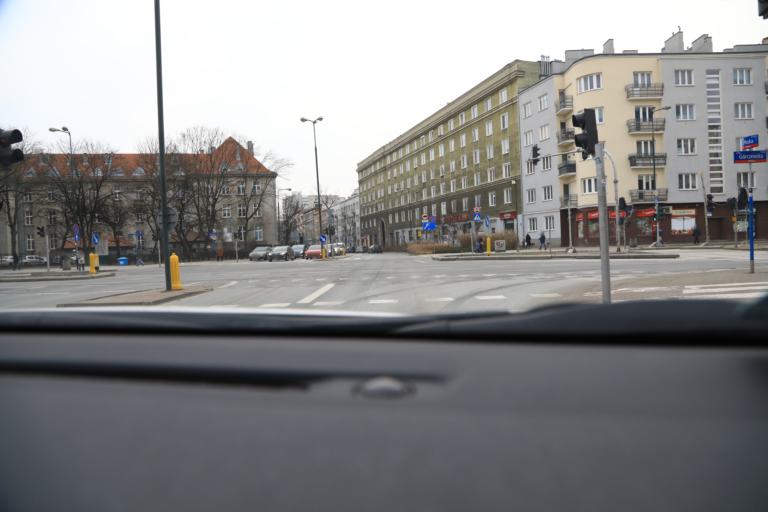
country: PL
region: Masovian Voivodeship
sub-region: Warszawa
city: Wola
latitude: 52.2376
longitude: 20.9652
